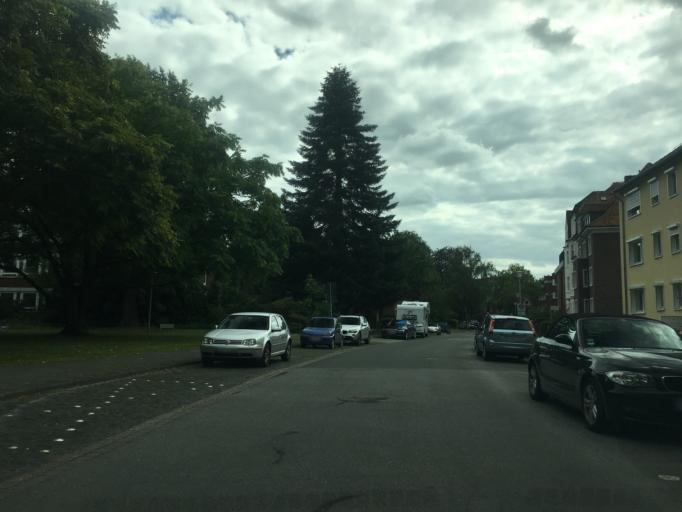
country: DE
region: North Rhine-Westphalia
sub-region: Regierungsbezirk Munster
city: Muenster
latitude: 51.9651
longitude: 7.6041
